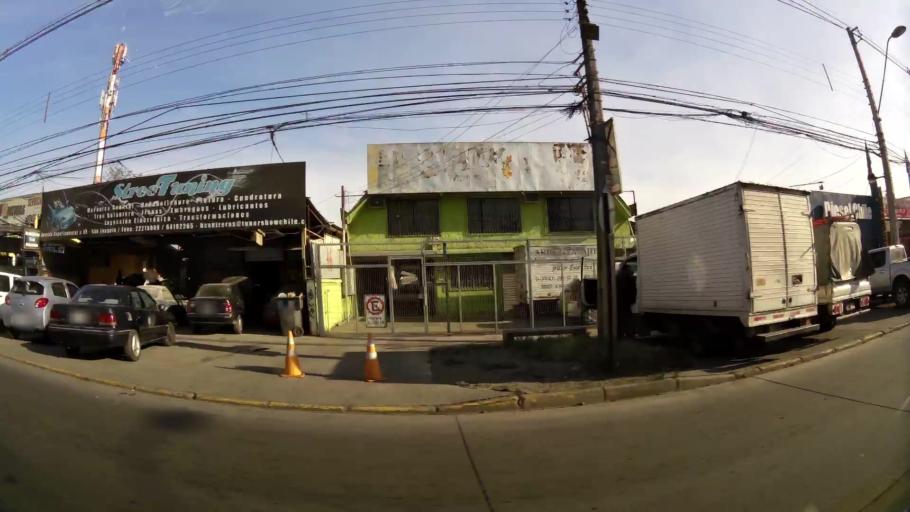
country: CL
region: Santiago Metropolitan
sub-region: Provincia de Santiago
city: Villa Presidente Frei, Nunoa, Santiago, Chile
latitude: -33.5082
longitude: -70.6152
